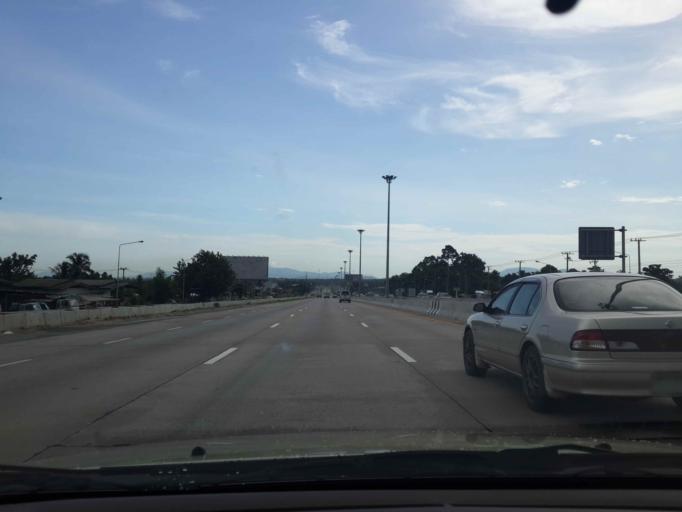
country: TH
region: Chon Buri
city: Ban Talat Bueng
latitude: 12.9953
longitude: 100.9907
